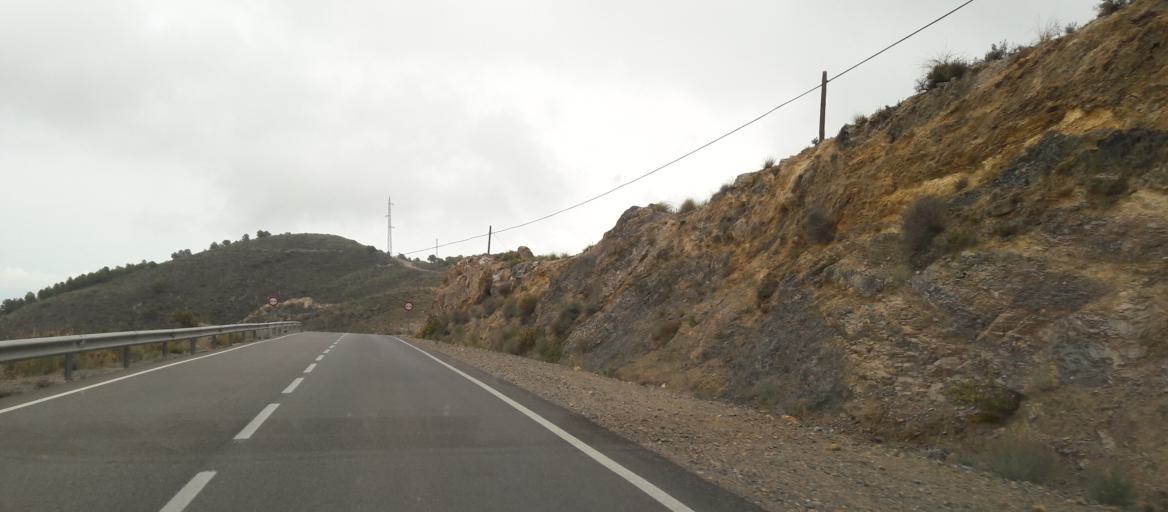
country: ES
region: Andalusia
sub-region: Provincia de Almeria
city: Enix
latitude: 36.8728
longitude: -2.6212
